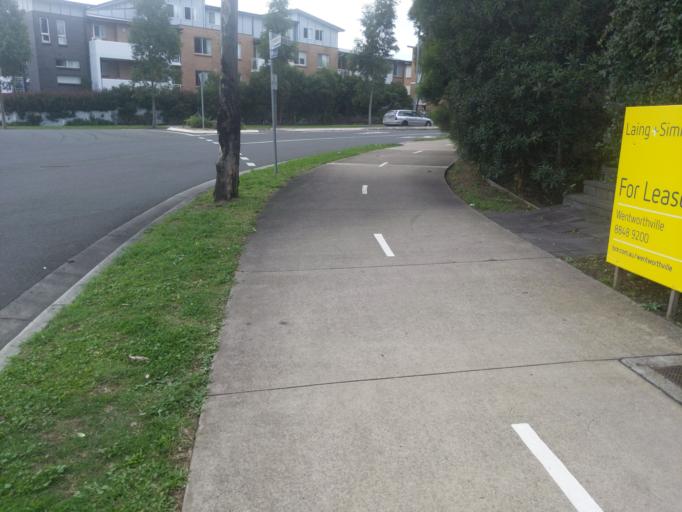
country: AU
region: New South Wales
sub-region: Holroyd
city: Girraween
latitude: -33.8172
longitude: 150.9316
